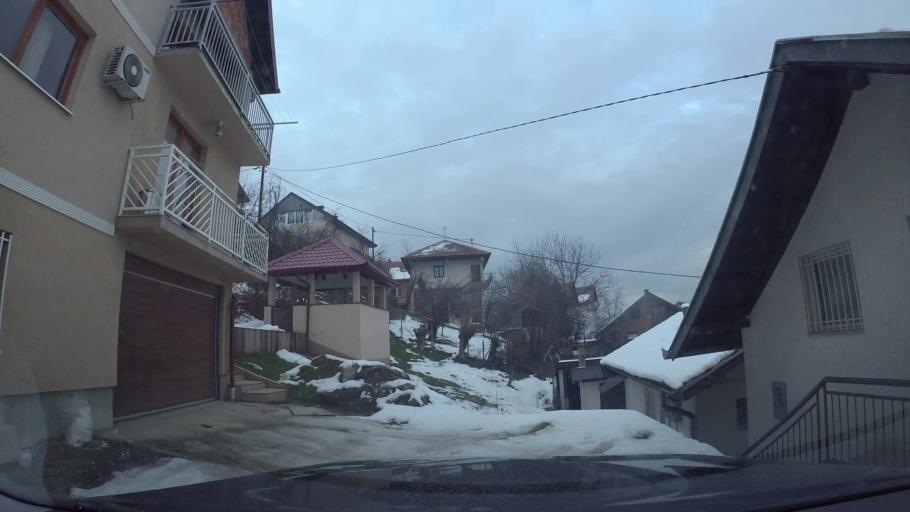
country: BA
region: Federation of Bosnia and Herzegovina
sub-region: Kanton Sarajevo
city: Sarajevo
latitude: 43.8561
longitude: 18.3596
